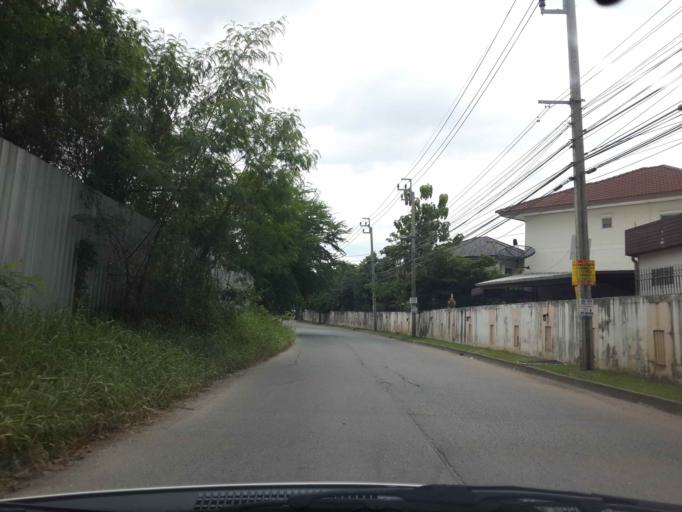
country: TH
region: Bangkok
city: Khlong Sam Wa
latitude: 13.8848
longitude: 100.7110
